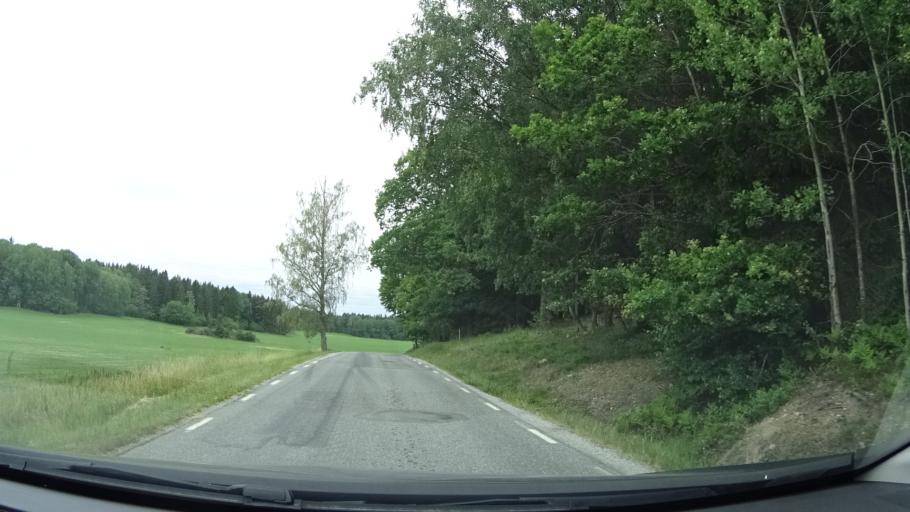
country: SE
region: Stockholm
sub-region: Varmdo Kommun
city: Mortnas
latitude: 59.3650
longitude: 18.4725
